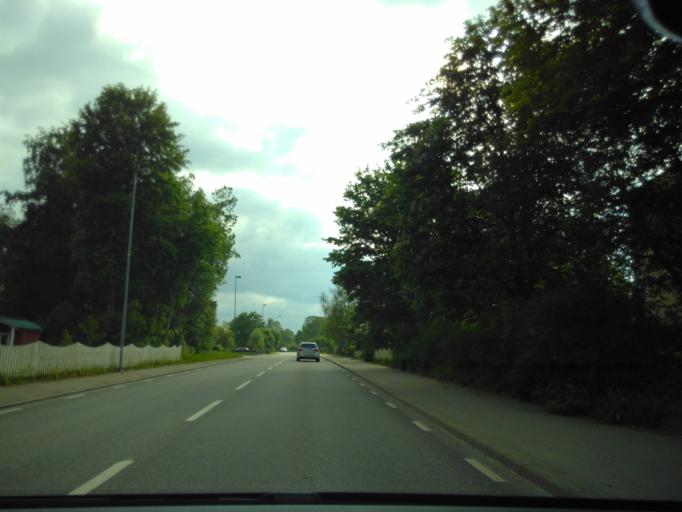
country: SE
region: Vaestra Goetaland
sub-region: Herrljunga Kommun
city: Herrljunga
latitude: 58.0779
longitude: 13.0103
